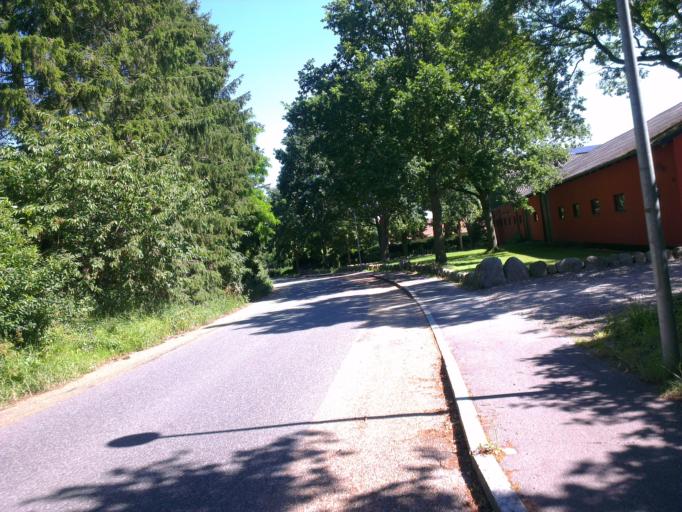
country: DK
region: Capital Region
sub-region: Frederikssund Kommune
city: Slangerup
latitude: 55.8308
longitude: 12.1736
